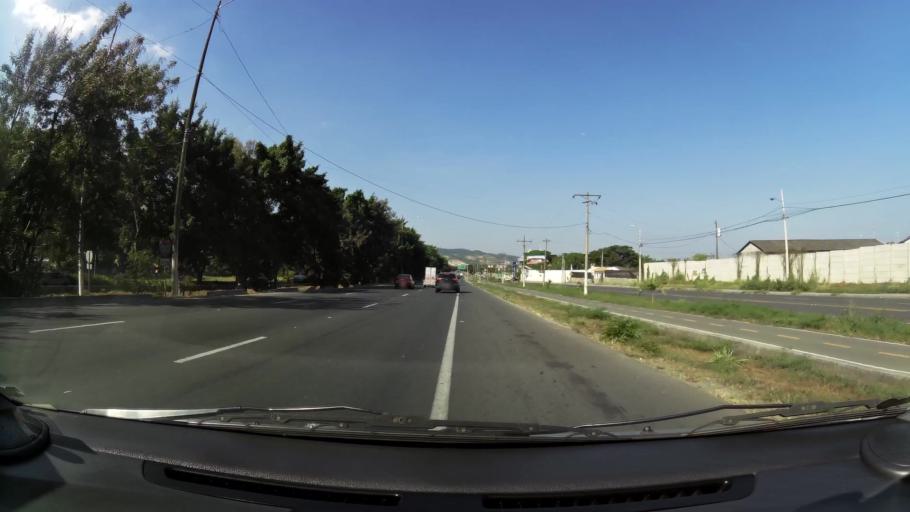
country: EC
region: Guayas
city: Santa Lucia
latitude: -2.1855
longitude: -80.0085
